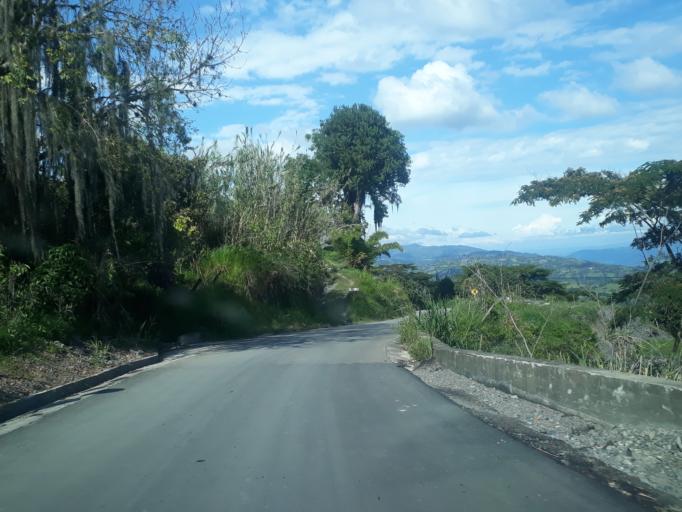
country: CO
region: Santander
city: Velez
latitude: 6.0342
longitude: -73.6538
